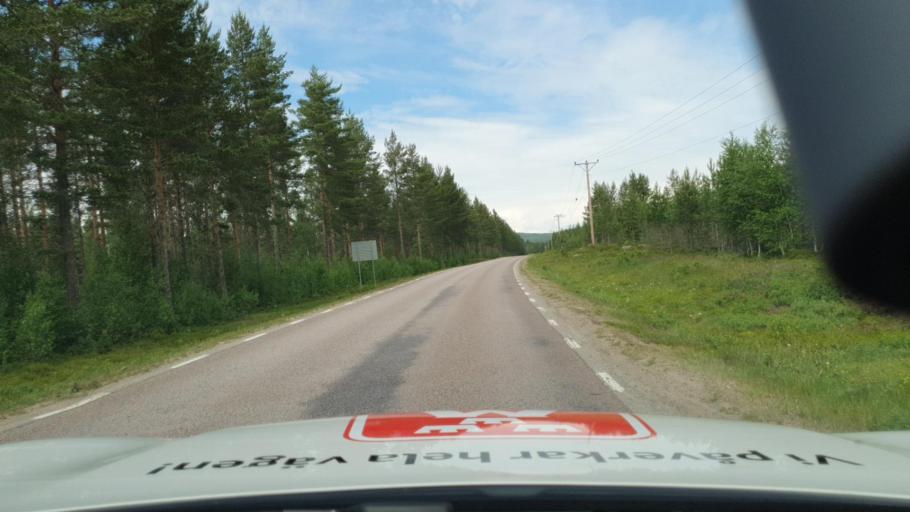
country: NO
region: Hedmark
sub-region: Grue
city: Kirkenaer
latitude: 60.7060
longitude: 12.6143
